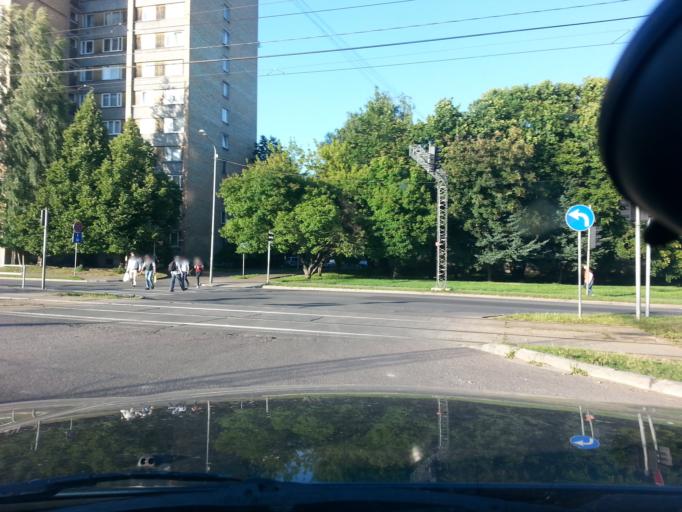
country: LV
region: Kekava
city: Balozi
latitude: 56.9179
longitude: 24.1734
